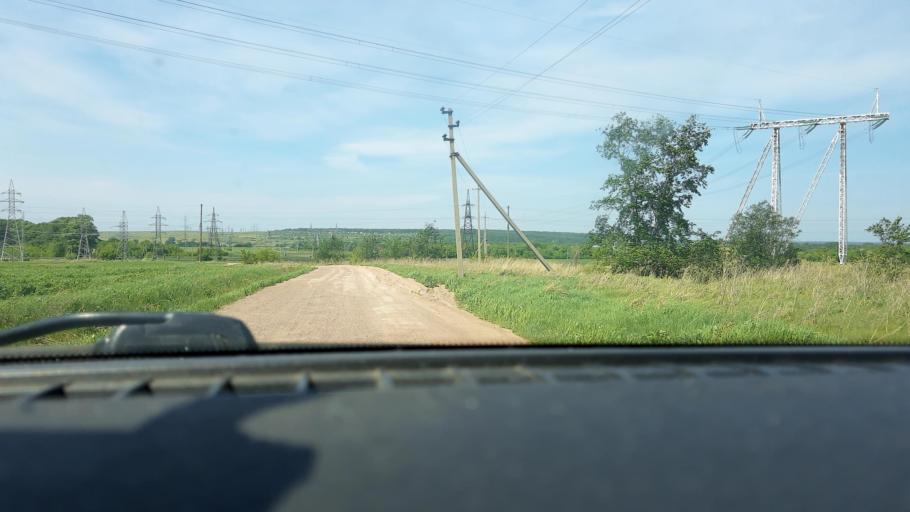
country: RU
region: Bashkortostan
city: Avdon
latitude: 54.4303
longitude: 55.8342
